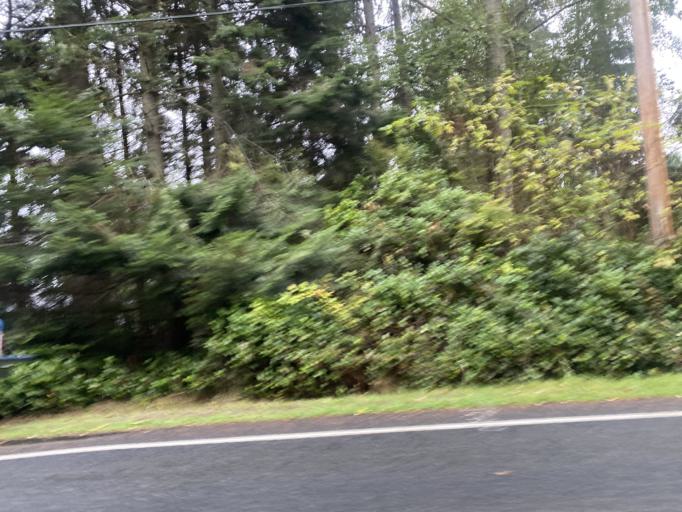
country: US
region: Washington
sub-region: Island County
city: Camano
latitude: 48.0952
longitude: -122.5189
